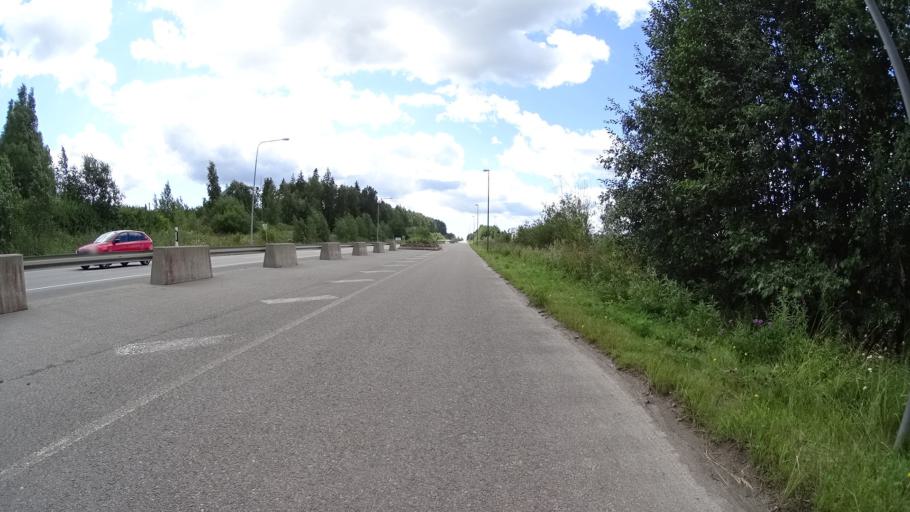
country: FI
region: Uusimaa
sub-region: Helsinki
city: Vantaa
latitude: 60.3309
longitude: 24.9236
